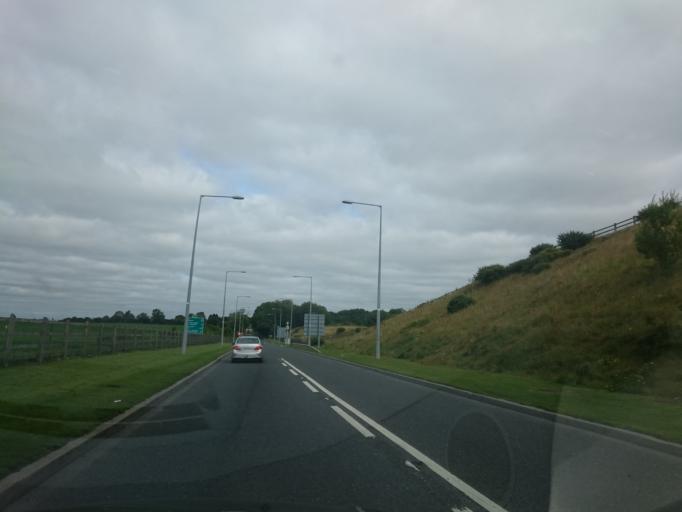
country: IE
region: Leinster
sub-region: Kilkenny
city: Kilkenny
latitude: 52.6776
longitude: -7.2537
